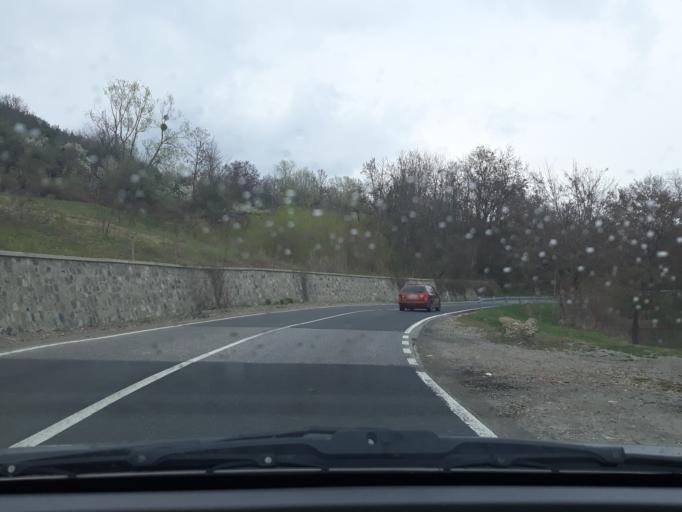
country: RO
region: Harghita
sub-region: Comuna Lupeni
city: Lupeni
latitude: 46.4112
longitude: 25.2193
